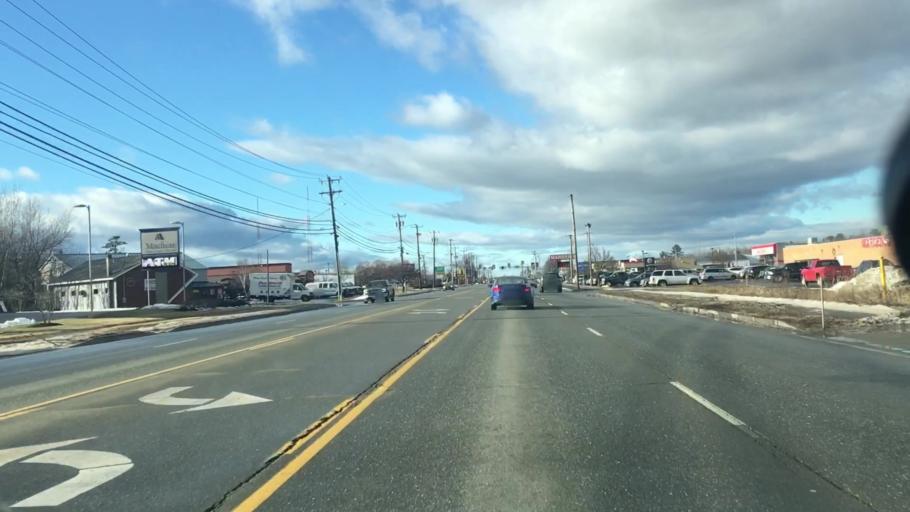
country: US
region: Maine
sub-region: Penobscot County
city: Brewer
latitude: 44.7789
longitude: -68.7391
